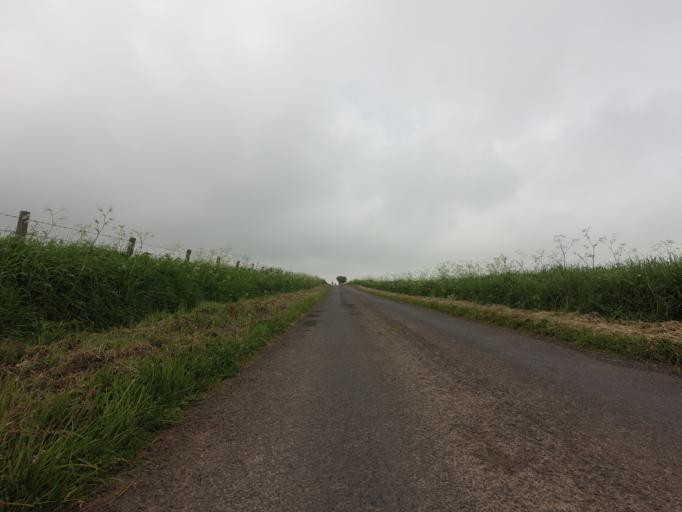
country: GB
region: Scotland
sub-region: Perth and Kinross
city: Milnathort
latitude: 56.2429
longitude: -3.3424
